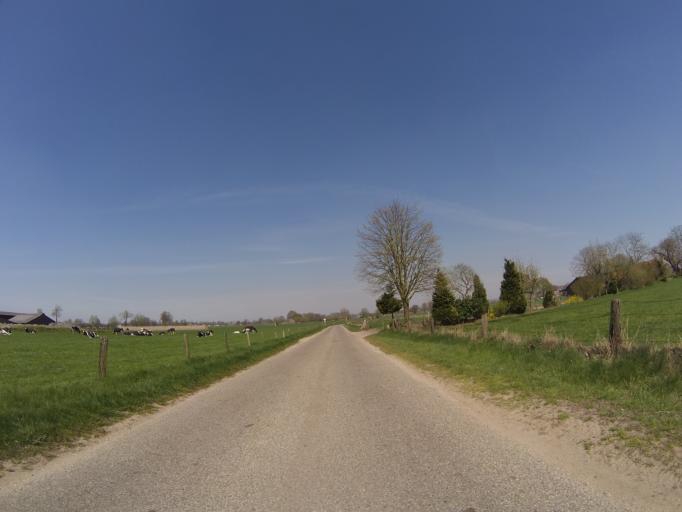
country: NL
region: Utrecht
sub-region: Gemeente Rhenen
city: Rhenen
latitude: 51.9640
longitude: 5.5998
